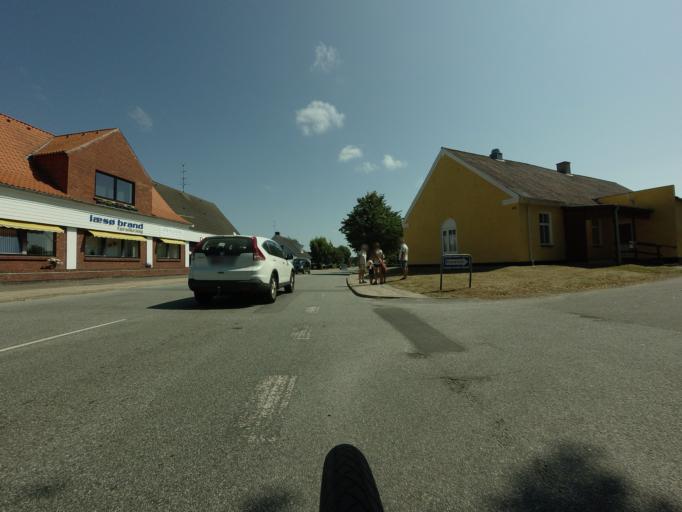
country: DK
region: North Denmark
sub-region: Laeso Kommune
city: Byrum
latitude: 57.2553
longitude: 11.0006
